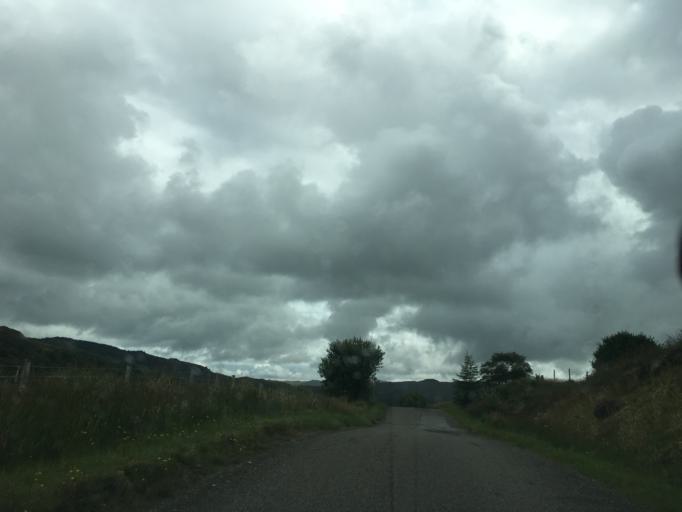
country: GB
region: Scotland
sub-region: Argyll and Bute
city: Oban
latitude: 56.2858
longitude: -5.3322
